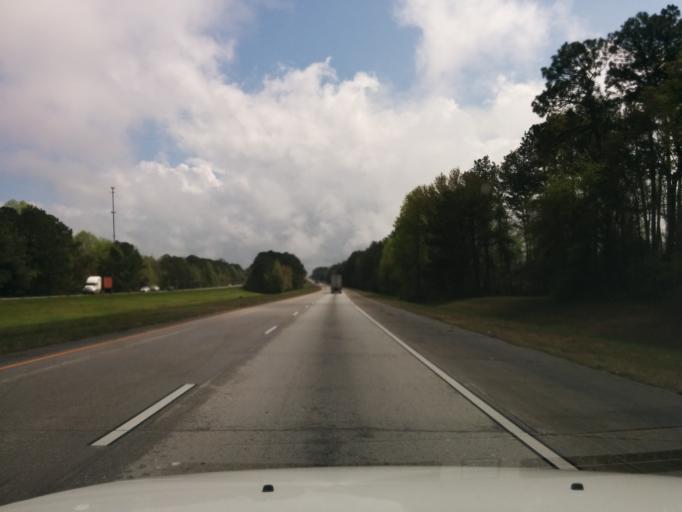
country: US
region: Georgia
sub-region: Candler County
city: Metter
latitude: 32.3485
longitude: -81.9740
